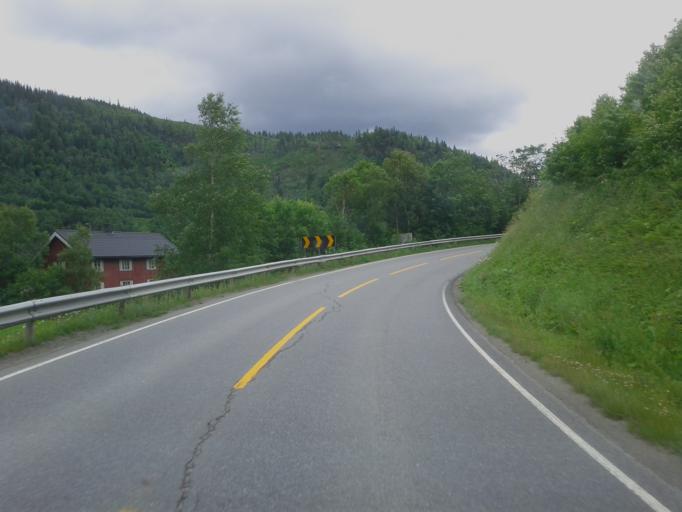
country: NO
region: Sor-Trondelag
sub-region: Midtre Gauldal
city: Storen
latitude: 62.9495
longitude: 10.6248
